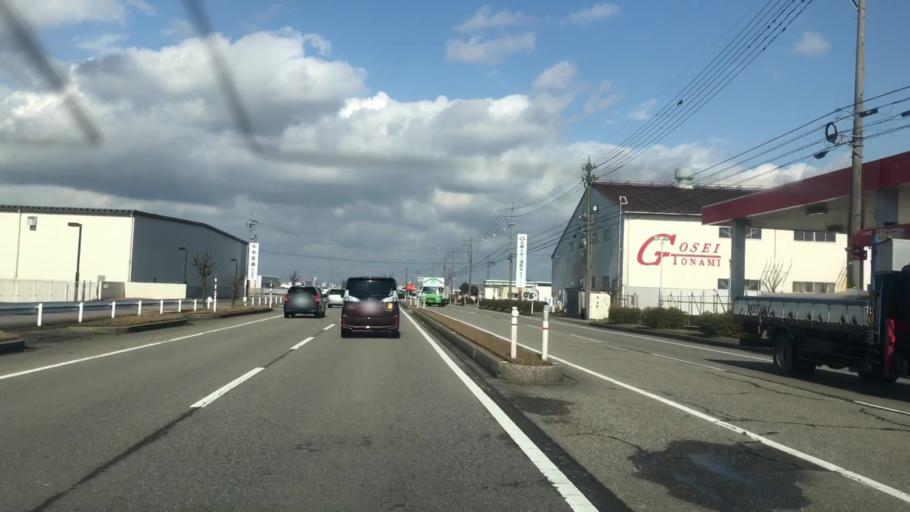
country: JP
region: Toyama
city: Kuragaki-kosugi
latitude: 36.7086
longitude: 137.0798
